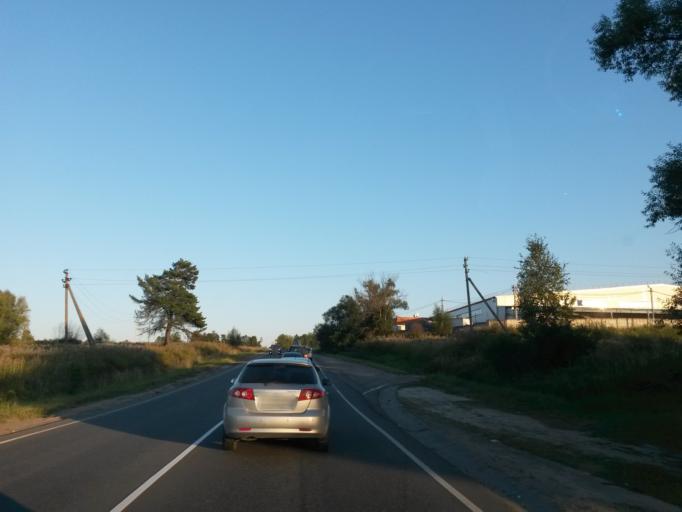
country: RU
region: Moskovskaya
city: Vostryakovo
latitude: 55.3563
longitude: 37.7420
